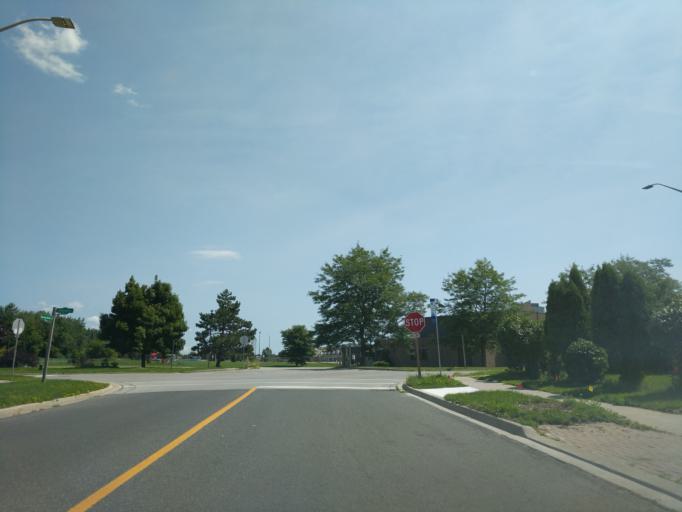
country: CA
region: Ontario
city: Markham
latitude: 43.8282
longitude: -79.3097
